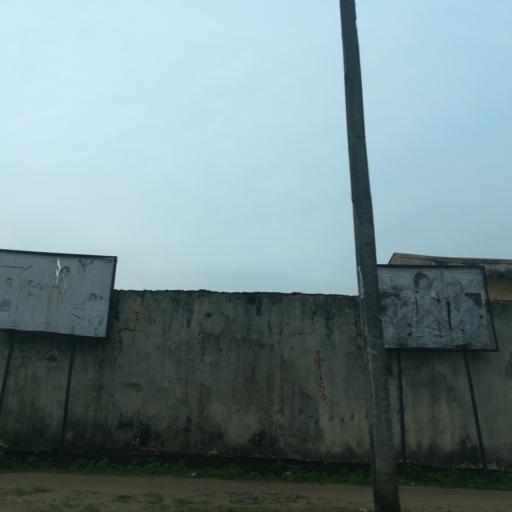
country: NG
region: Rivers
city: Port Harcourt
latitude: 4.7647
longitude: 7.0133
